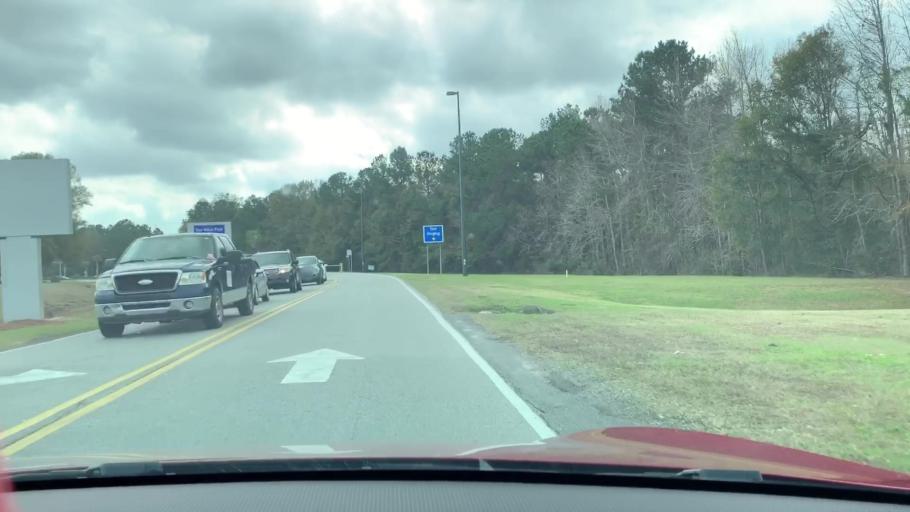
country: US
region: Georgia
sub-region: Chatham County
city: Pooler
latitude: 32.1380
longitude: -81.2154
